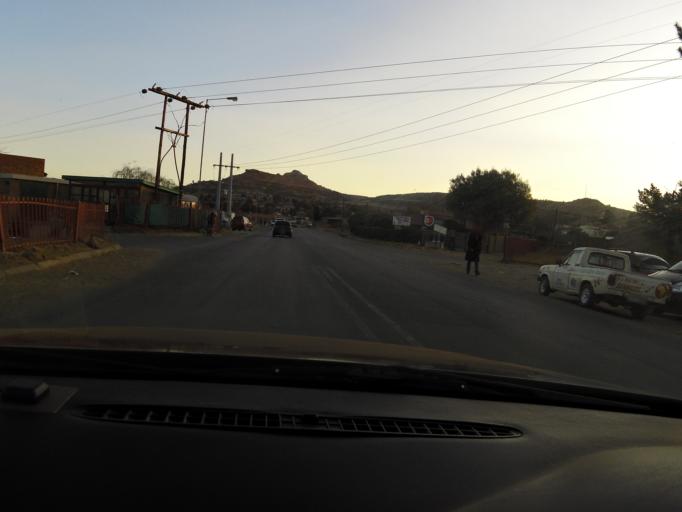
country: LS
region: Maseru
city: Maseru
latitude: -29.3150
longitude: 27.5106
